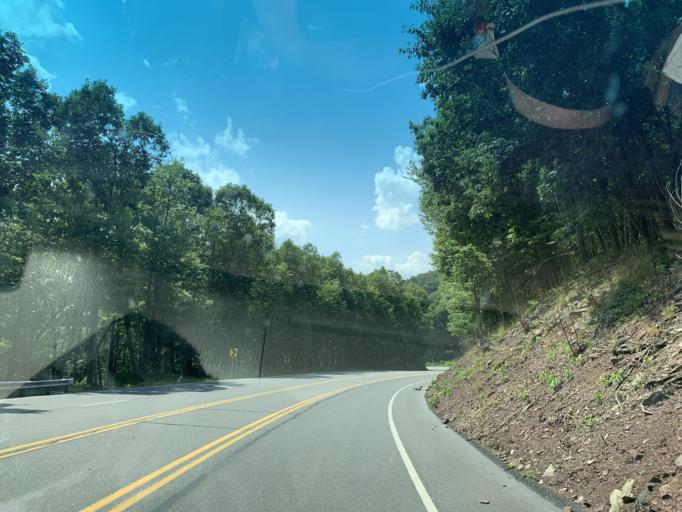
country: US
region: Pennsylvania
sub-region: Schuylkill County
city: Girardville
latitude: 40.7770
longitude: -76.2685
